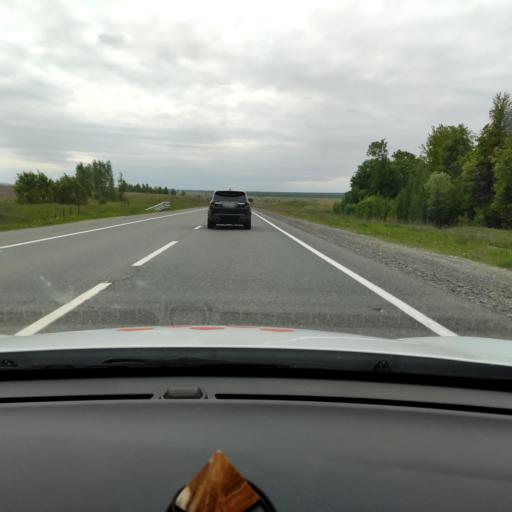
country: RU
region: Tatarstan
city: Pestretsy
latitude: 55.5855
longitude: 49.7171
